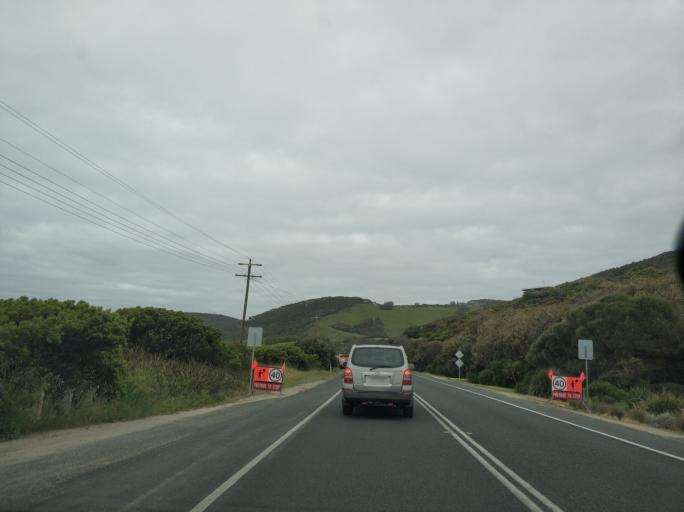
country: AU
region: Victoria
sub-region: Surf Coast
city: Anglesea
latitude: -38.4722
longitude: 144.0437
